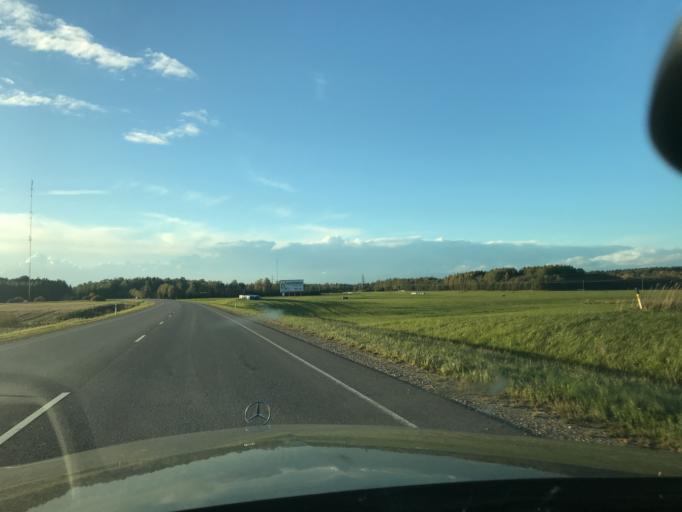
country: EE
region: Vorumaa
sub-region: Voru linn
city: Voru
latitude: 57.8565
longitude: 27.0199
